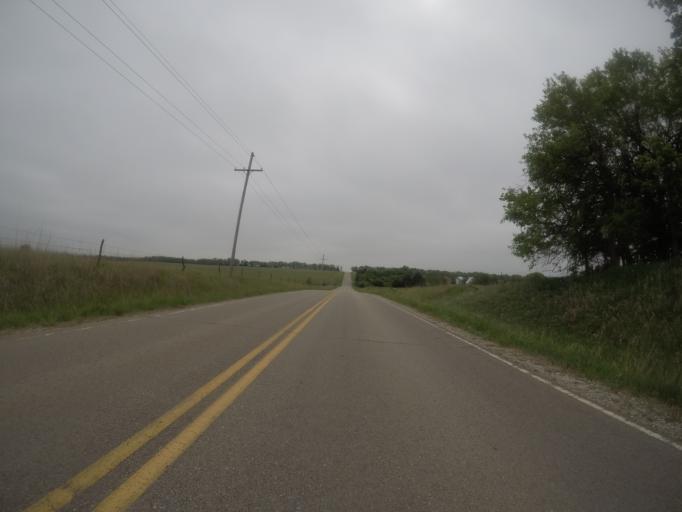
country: US
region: Kansas
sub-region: Pottawatomie County
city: Westmoreland
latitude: 39.5221
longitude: -96.2909
